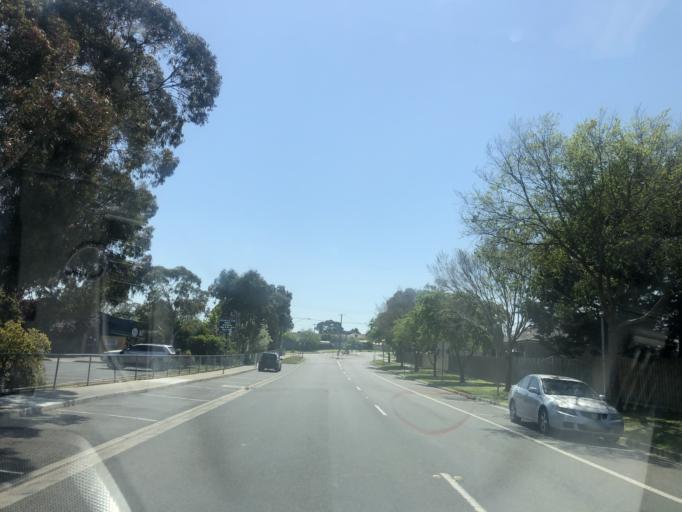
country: AU
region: Victoria
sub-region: Casey
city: Narre Warren South
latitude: -38.0342
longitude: 145.2798
